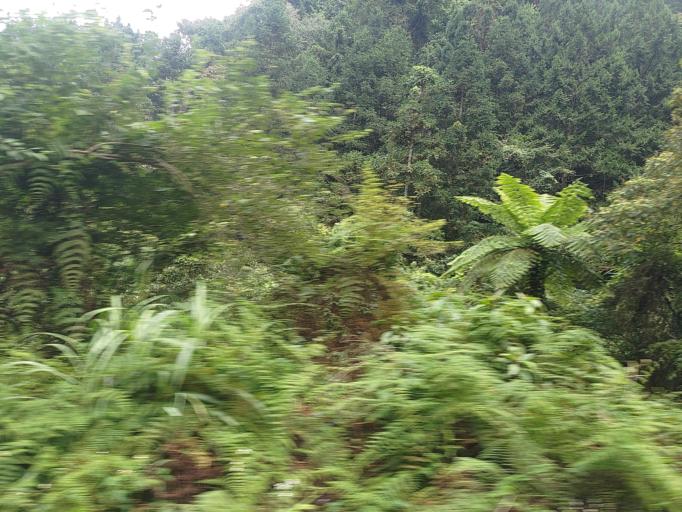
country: TW
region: Taiwan
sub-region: Hsinchu
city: Hsinchu
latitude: 24.6309
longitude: 121.0757
